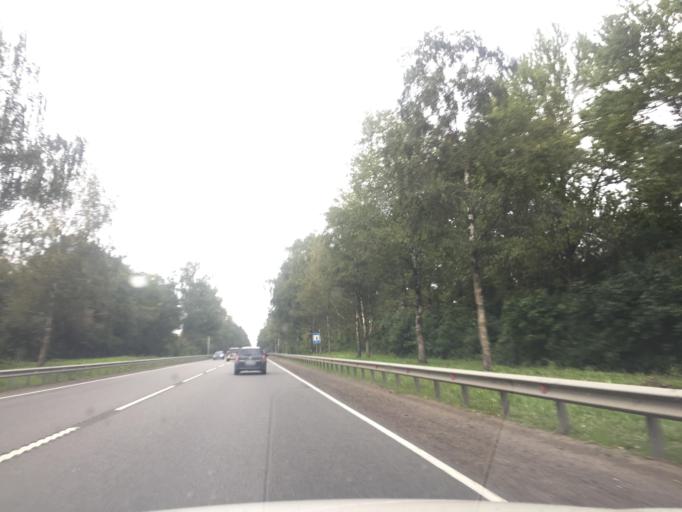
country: RU
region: Leningrad
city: Voyskovitsy
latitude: 59.4765
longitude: 30.0163
